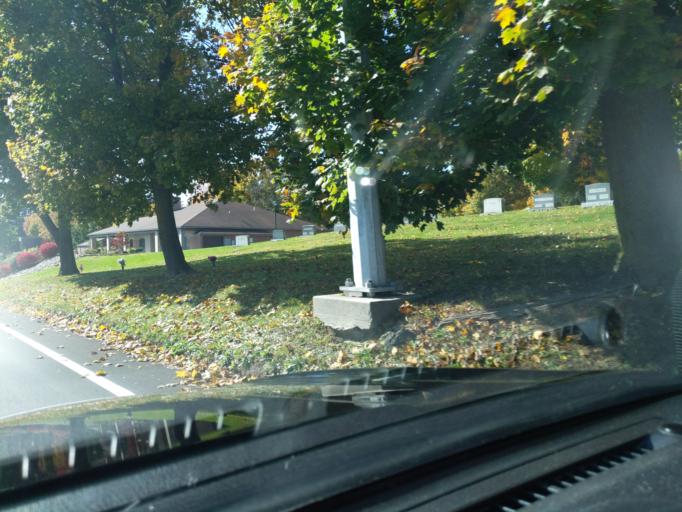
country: US
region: Pennsylvania
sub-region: Blair County
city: Lakemont
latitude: 40.4567
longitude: -78.4098
